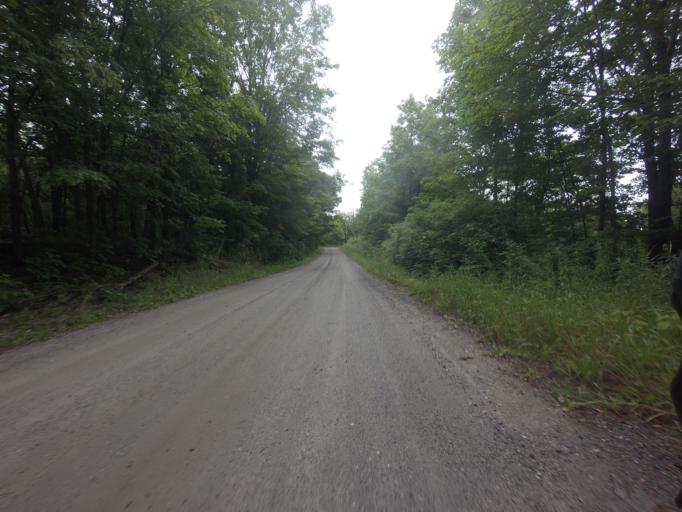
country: CA
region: Ontario
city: Perth
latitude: 45.0476
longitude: -76.3956
